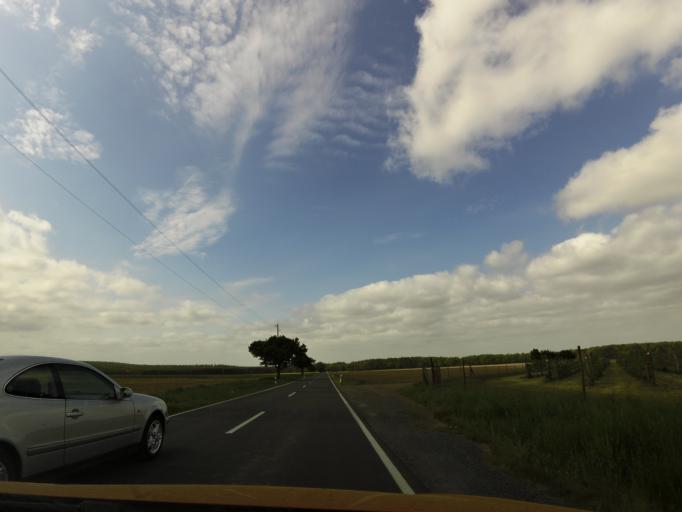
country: DE
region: Brandenburg
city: Gorzke
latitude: 52.1027
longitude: 12.3535
